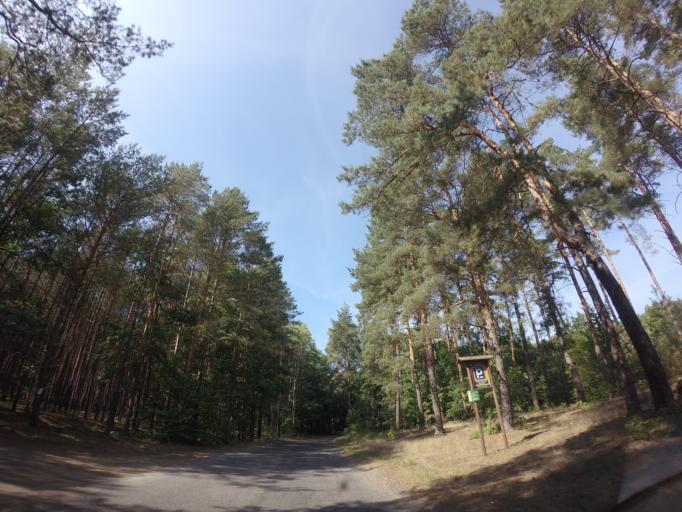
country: PL
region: Lubusz
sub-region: Powiat strzelecko-drezdenecki
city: Stare Kurowo
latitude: 52.7557
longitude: 15.7391
